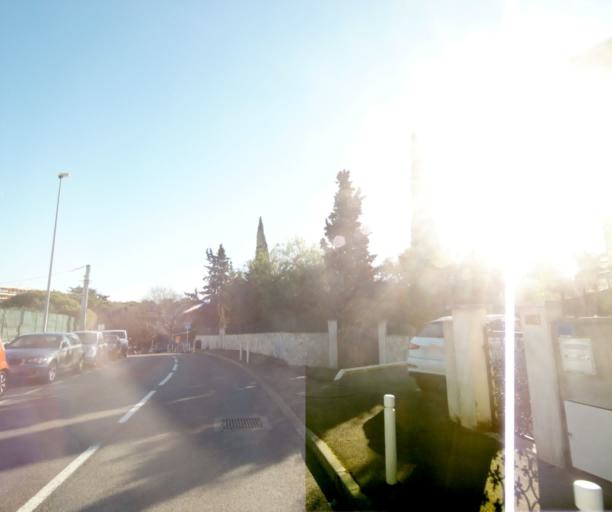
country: FR
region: Provence-Alpes-Cote d'Azur
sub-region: Departement des Alpes-Maritimes
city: Antibes
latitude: 43.5865
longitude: 7.1024
